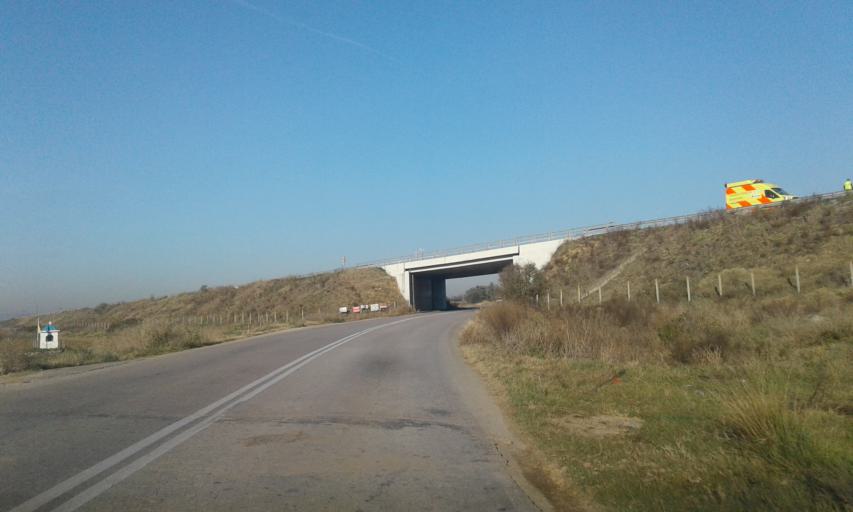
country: GR
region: Central Macedonia
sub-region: Nomos Thessalonikis
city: Kolchikon
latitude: 40.7089
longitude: 23.1826
